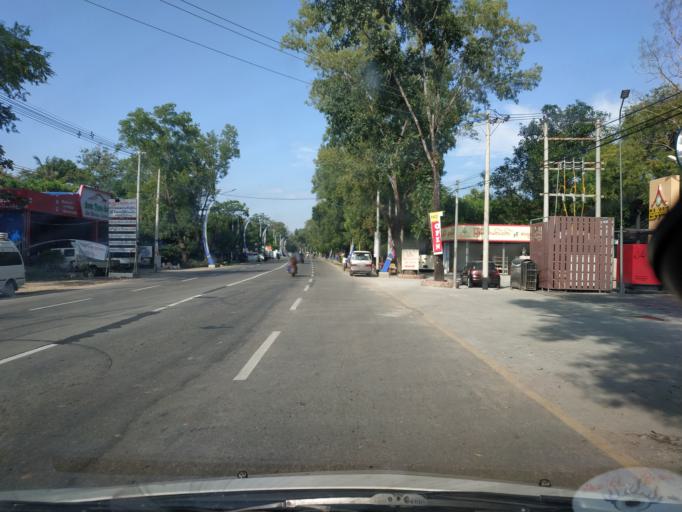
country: MM
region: Ayeyarwady
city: Pathein
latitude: 16.8020
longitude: 94.7673
